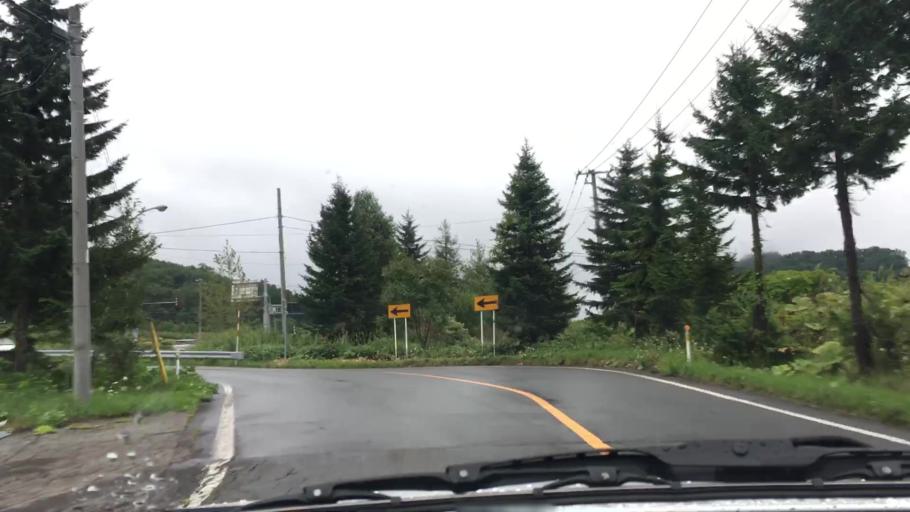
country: JP
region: Hokkaido
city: Niseko Town
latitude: 42.6094
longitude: 140.7275
